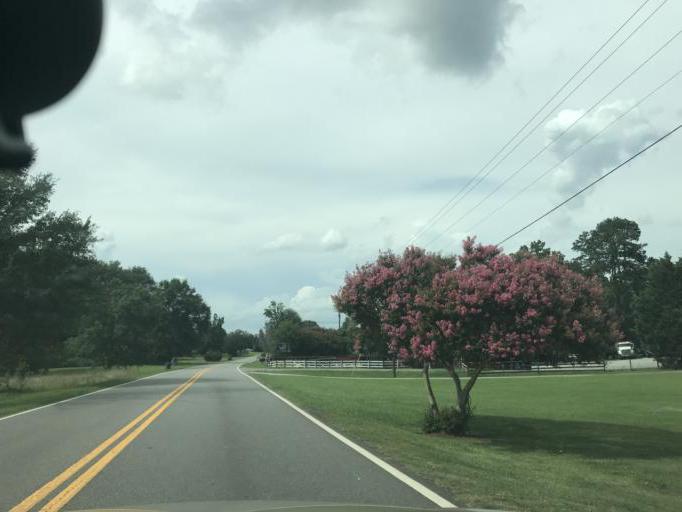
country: US
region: Georgia
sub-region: Forsyth County
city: Cumming
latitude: 34.2561
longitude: -84.2388
